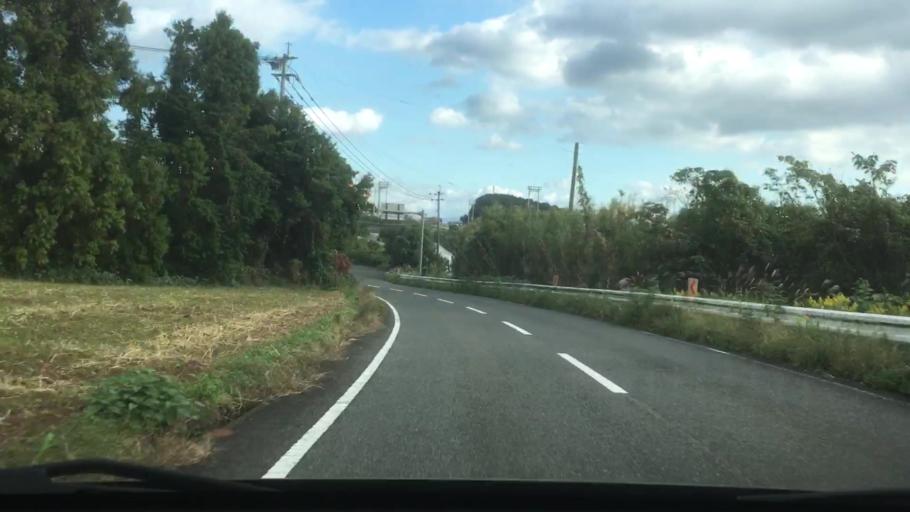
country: JP
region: Nagasaki
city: Sasebo
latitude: 33.0406
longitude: 129.6956
